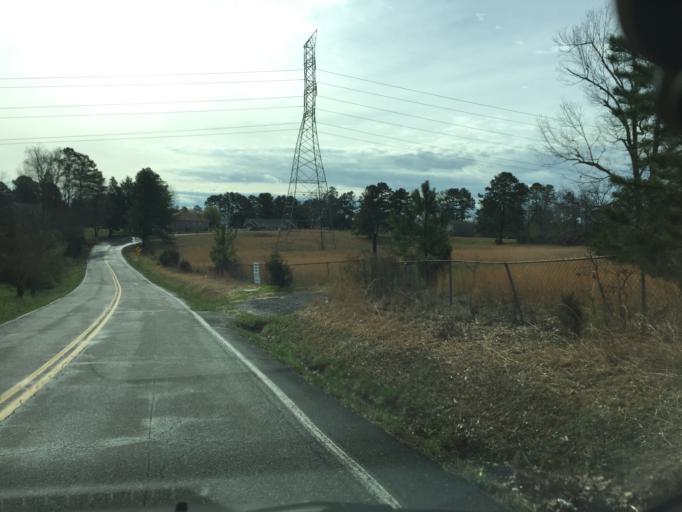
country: US
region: Tennessee
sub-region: Hamilton County
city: Collegedale
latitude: 35.0578
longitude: -85.1010
